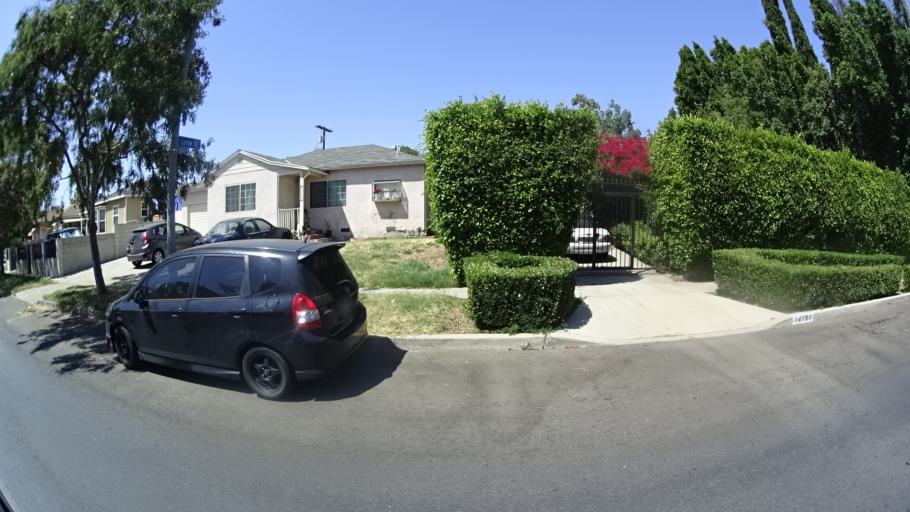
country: US
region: California
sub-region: Los Angeles County
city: Van Nuys
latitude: 34.2170
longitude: -118.4419
